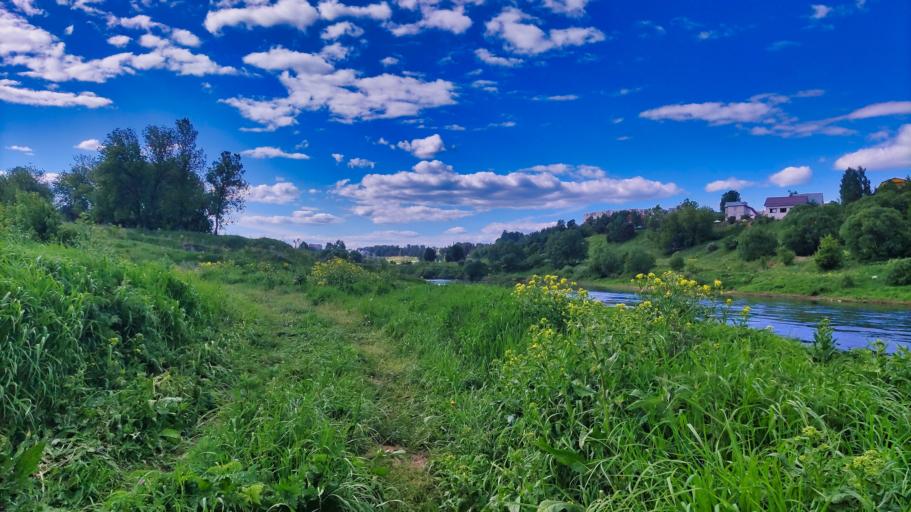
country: RU
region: Tverskaya
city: Rzhev
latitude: 56.2506
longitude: 34.3480
